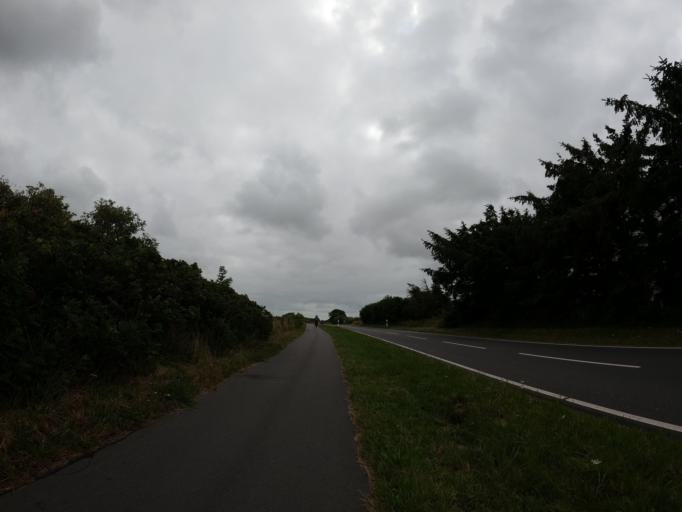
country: DE
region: Schleswig-Holstein
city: Tinnum
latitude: 54.9449
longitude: 8.3475
